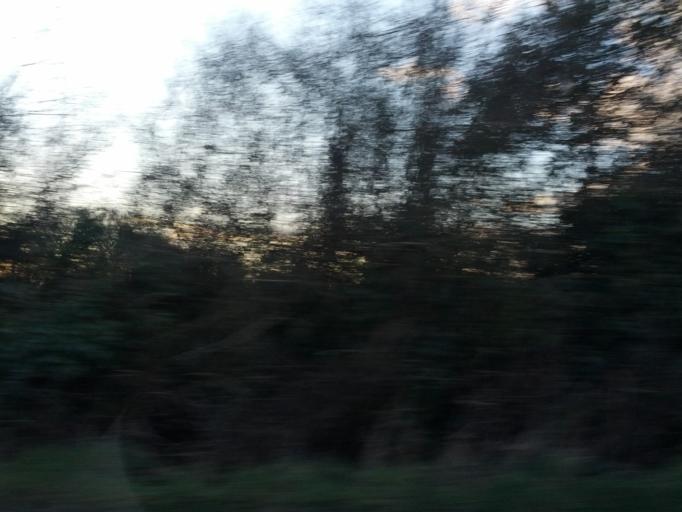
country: IE
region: Connaught
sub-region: County Galway
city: Athenry
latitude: 53.3018
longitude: -8.6250
